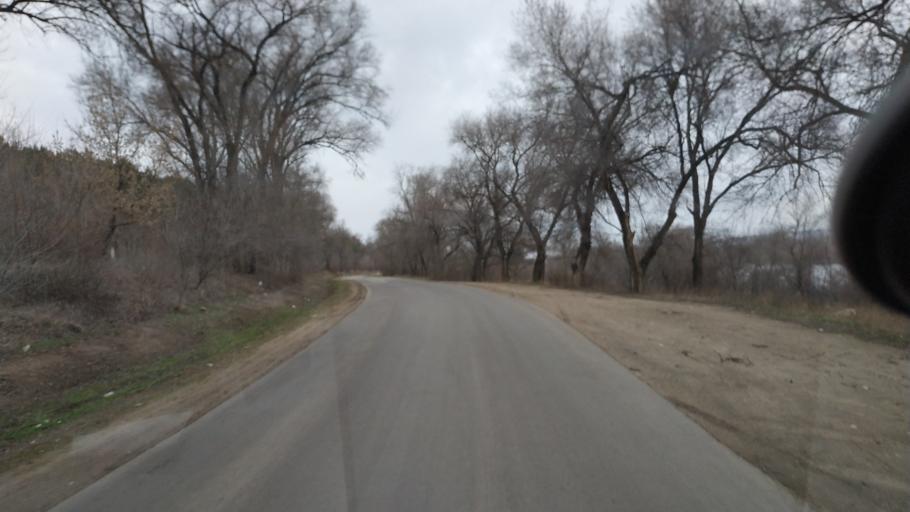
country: MD
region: Criuleni
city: Criuleni
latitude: 47.2267
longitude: 29.1614
